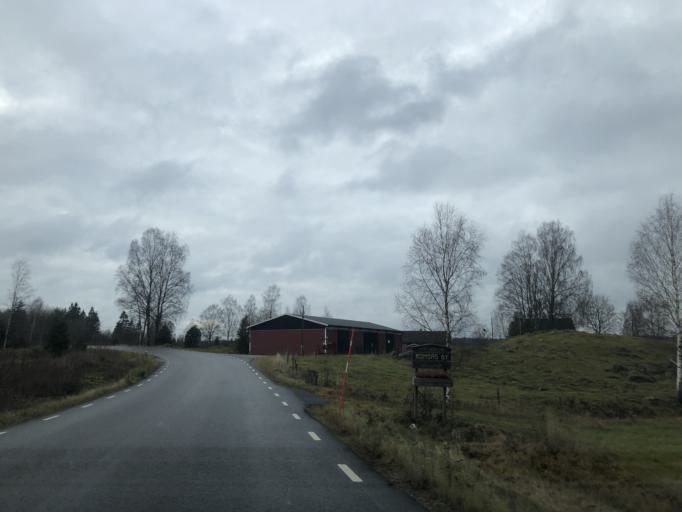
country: SE
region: Vaestra Goetaland
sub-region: Ulricehamns Kommun
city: Ulricehamn
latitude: 57.8342
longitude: 13.2659
